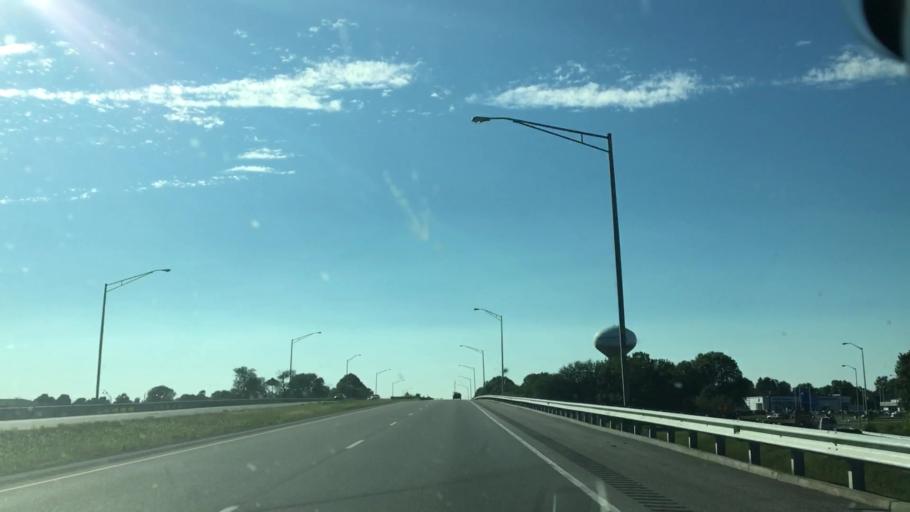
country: US
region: Kentucky
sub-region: Daviess County
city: Owensboro
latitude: 37.7282
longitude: -87.1198
